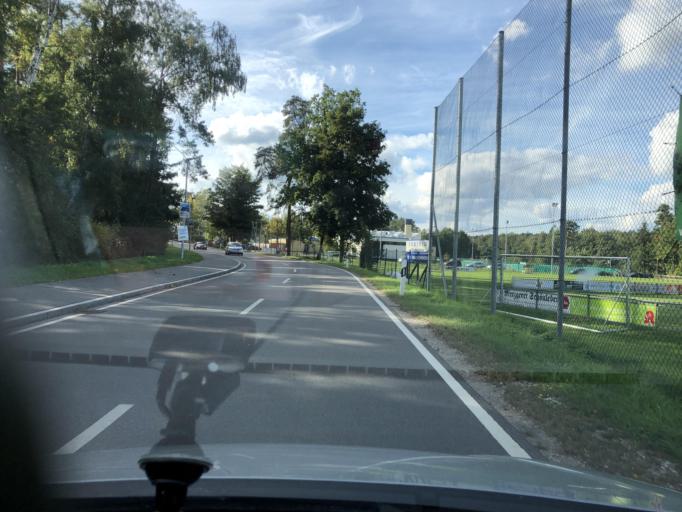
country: DE
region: Bavaria
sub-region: Regierungsbezirk Mittelfranken
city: Seukendorf
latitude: 49.4614
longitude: 10.8983
